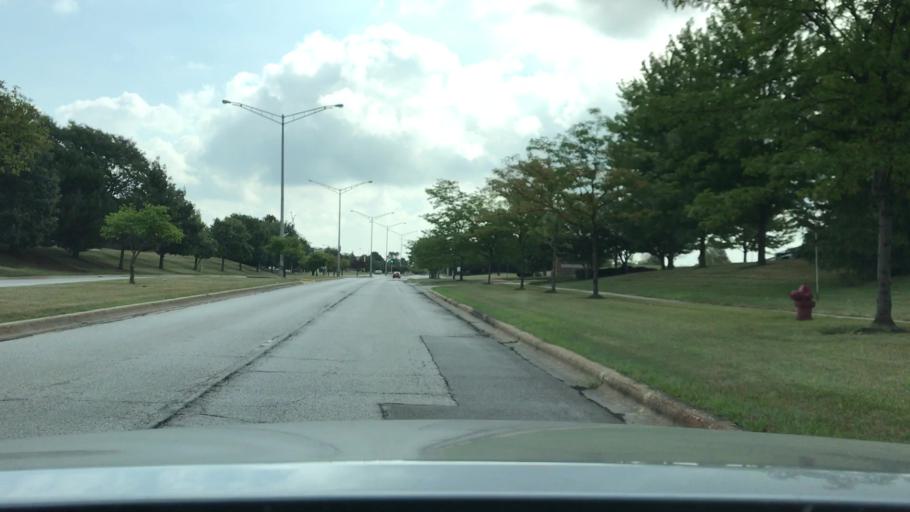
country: US
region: Illinois
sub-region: DuPage County
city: Warrenville
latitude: 41.7546
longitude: -88.2222
